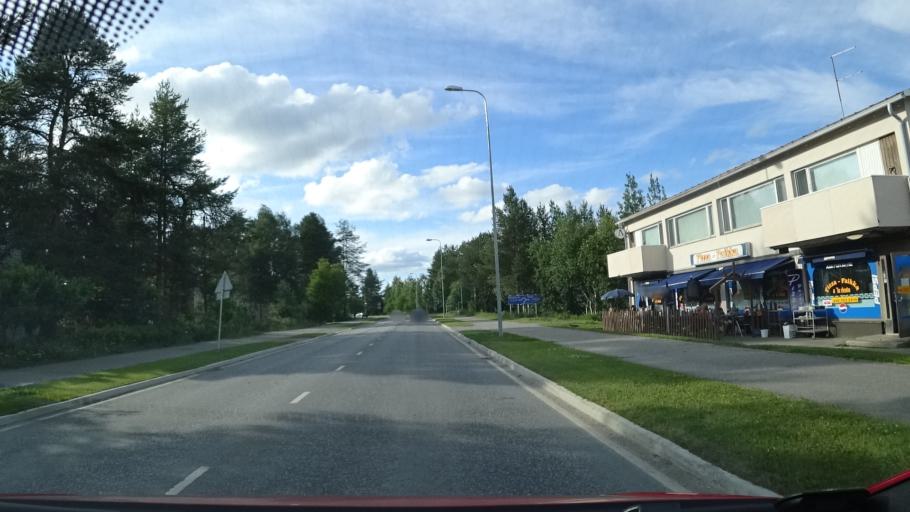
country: FI
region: Lapland
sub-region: Pohjois-Lappi
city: Sodankylae
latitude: 67.4200
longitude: 26.5906
